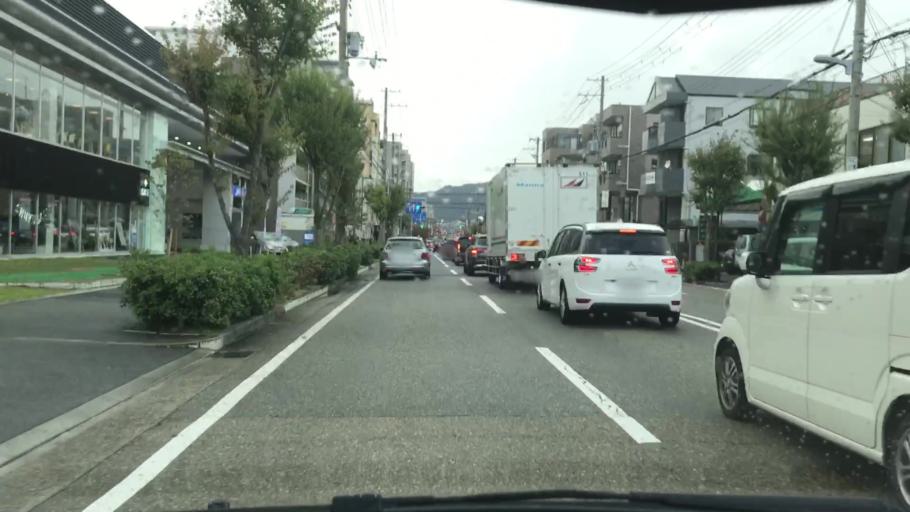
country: JP
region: Hyogo
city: Nishinomiya-hama
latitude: 34.7419
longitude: 135.3418
